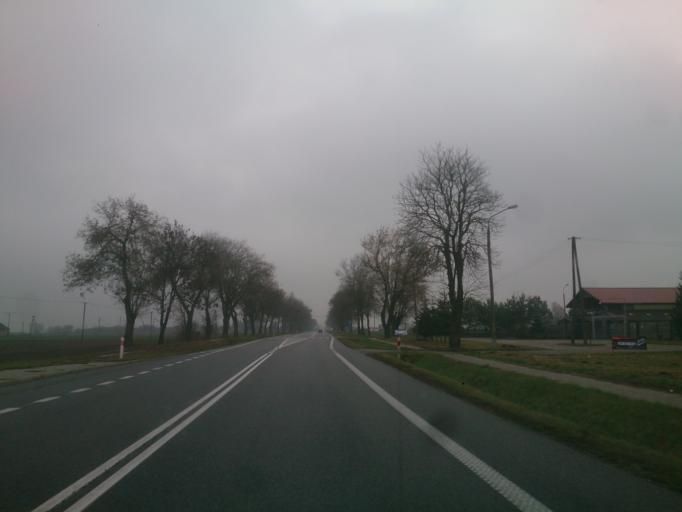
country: PL
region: Masovian Voivodeship
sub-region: Powiat sierpecki
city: Sierpc
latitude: 52.8424
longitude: 19.7231
